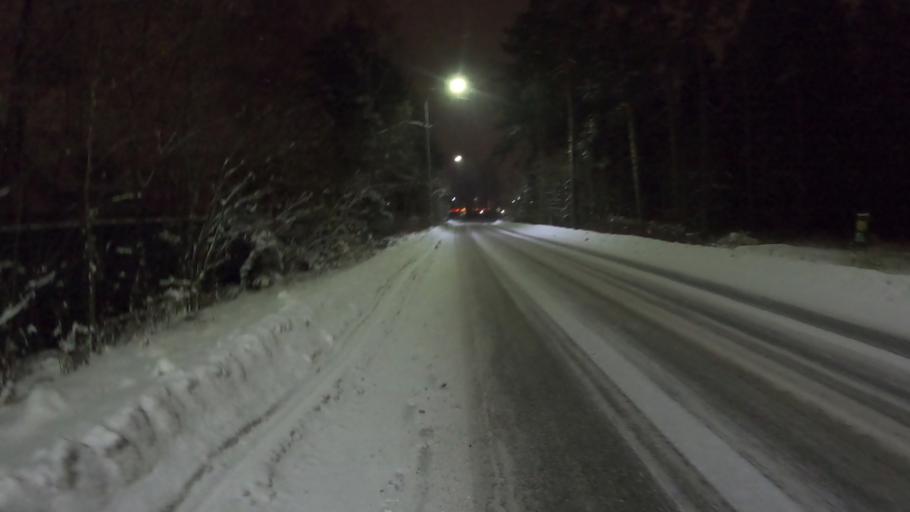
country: RU
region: Moskovskaya
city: Opalikha
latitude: 55.8424
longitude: 37.2232
